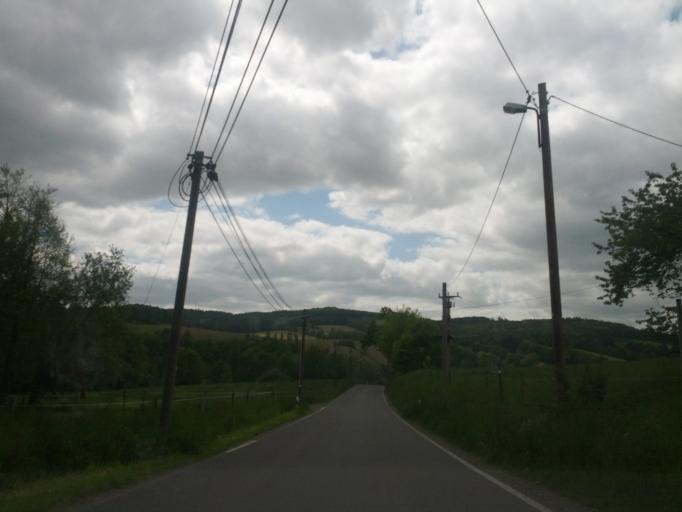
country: DE
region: Saxony
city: Kreischa
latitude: 50.9353
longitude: 13.7802
